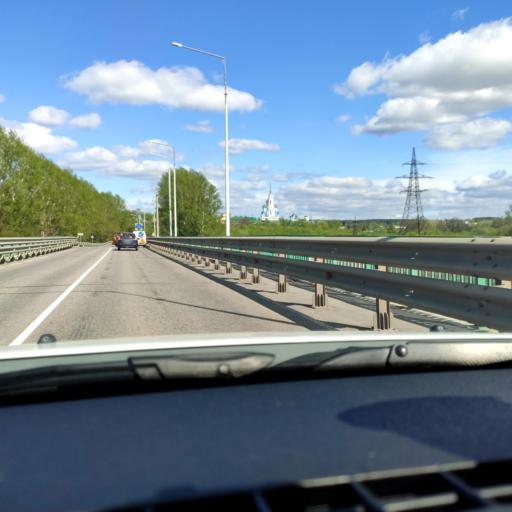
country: RU
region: Lipetsk
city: Zadonsk
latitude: 52.3944
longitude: 38.9059
